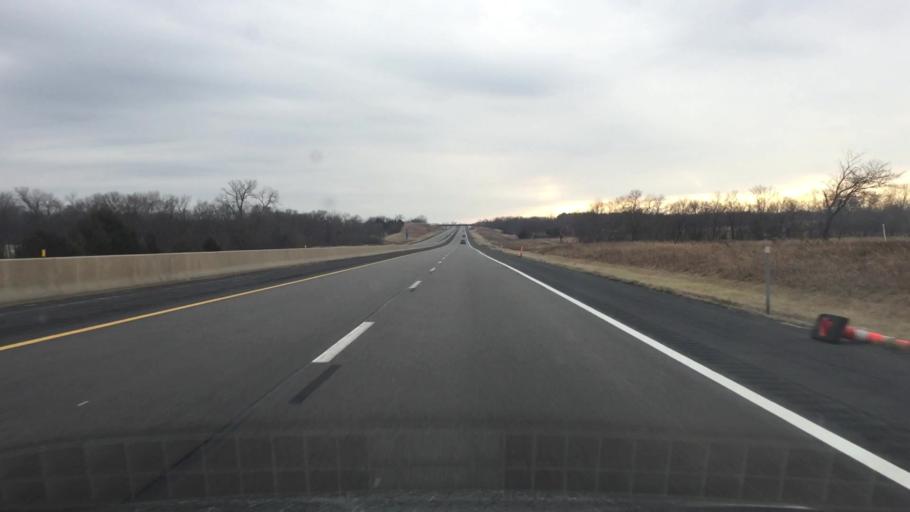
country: US
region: Kansas
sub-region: Osage County
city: Osage City
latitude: 38.7342
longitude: -95.9572
